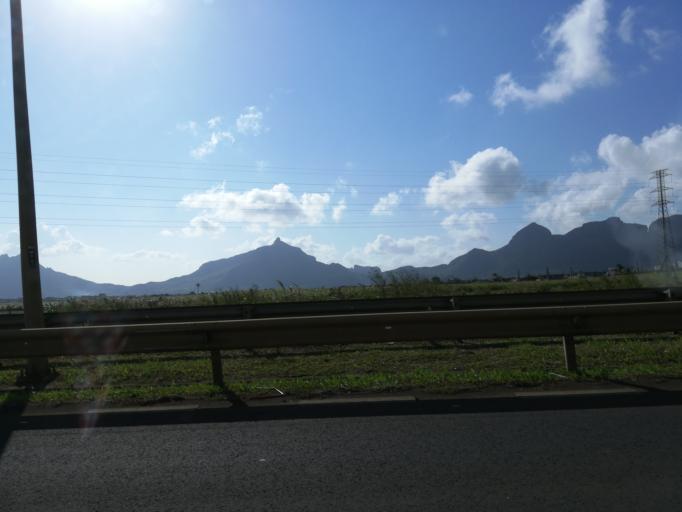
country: MU
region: Moka
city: Verdun
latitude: -20.2251
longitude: 57.5572
